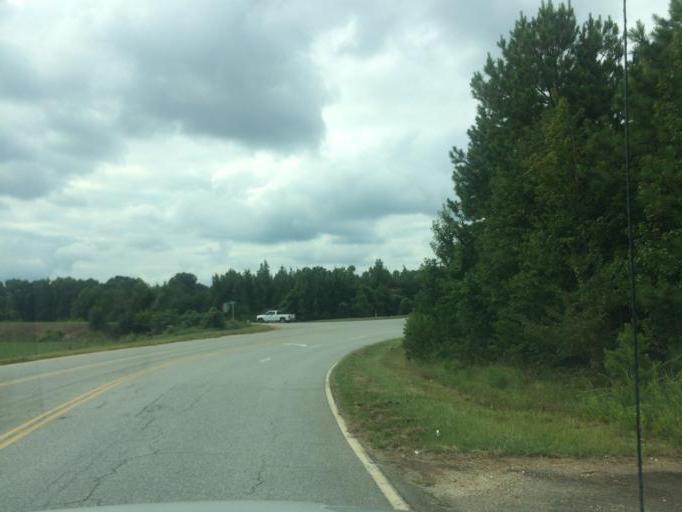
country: US
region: South Carolina
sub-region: Greenville County
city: Gantt
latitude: 34.7989
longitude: -82.4258
